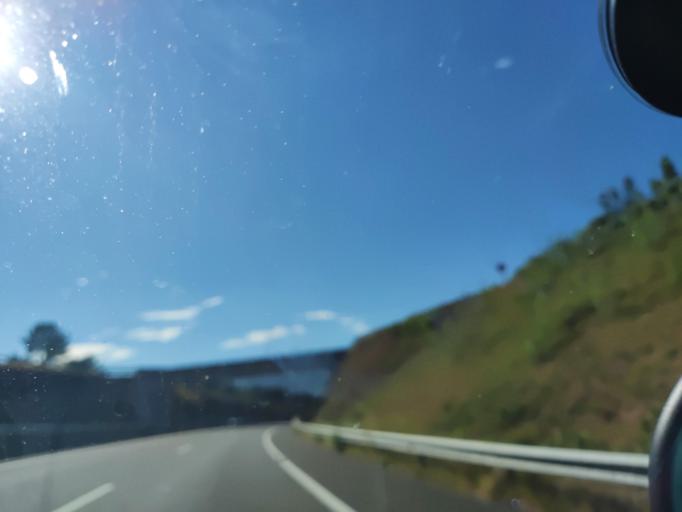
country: ES
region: Galicia
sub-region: Provincia da Coruna
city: Boiro
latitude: 42.6572
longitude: -8.8796
